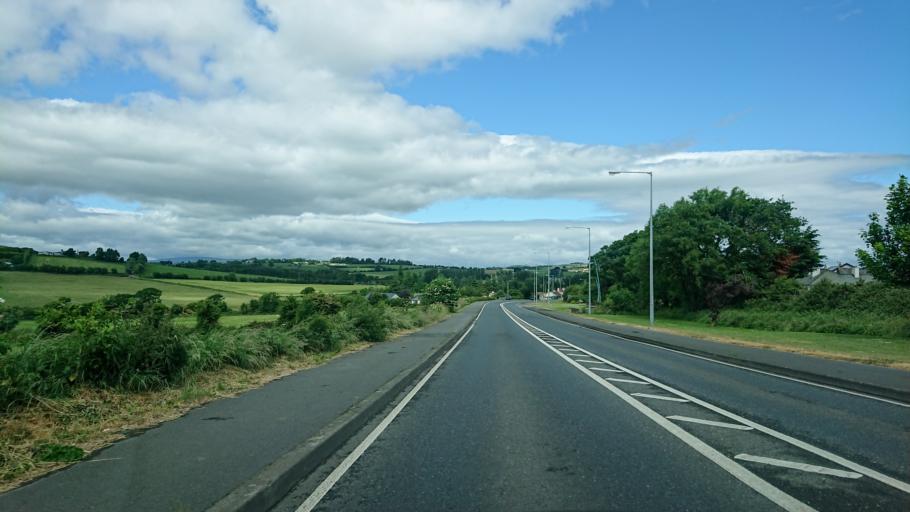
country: IE
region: Leinster
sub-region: Kilkenny
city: Mooncoin
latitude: 52.2277
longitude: -7.2345
